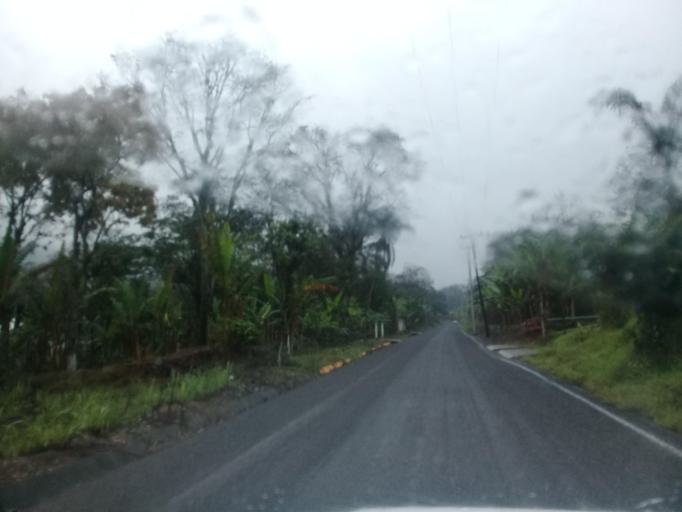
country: MX
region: Veracruz
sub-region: Amatlan de los Reyes
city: Centro de Readaptacion Social
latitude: 18.7990
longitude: -96.9379
